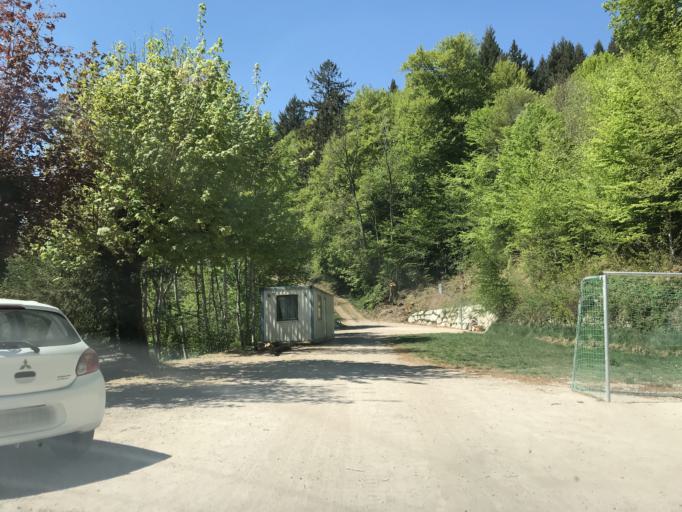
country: DE
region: Baden-Wuerttemberg
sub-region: Freiburg Region
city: Hasel
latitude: 47.6828
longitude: 7.8799
